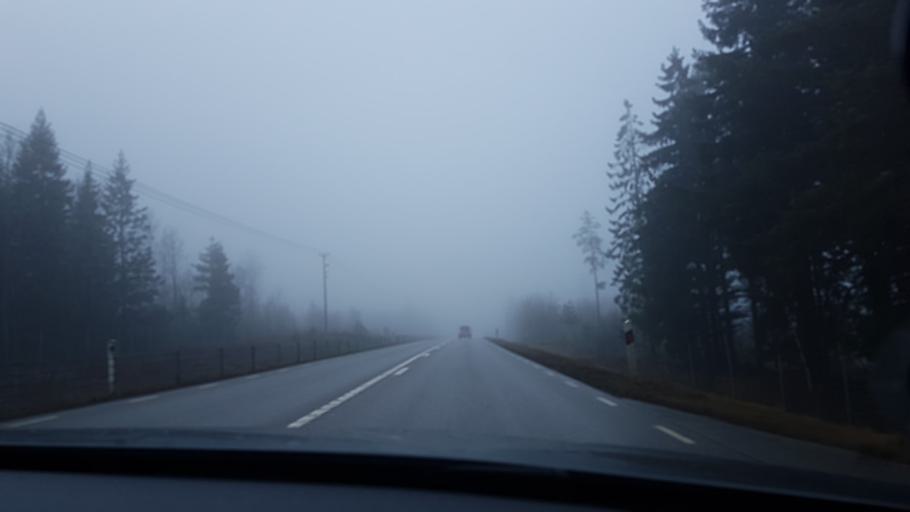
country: SE
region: Vaestra Goetaland
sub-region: Gullspangs Kommun
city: Gullspang
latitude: 58.9513
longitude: 14.0532
